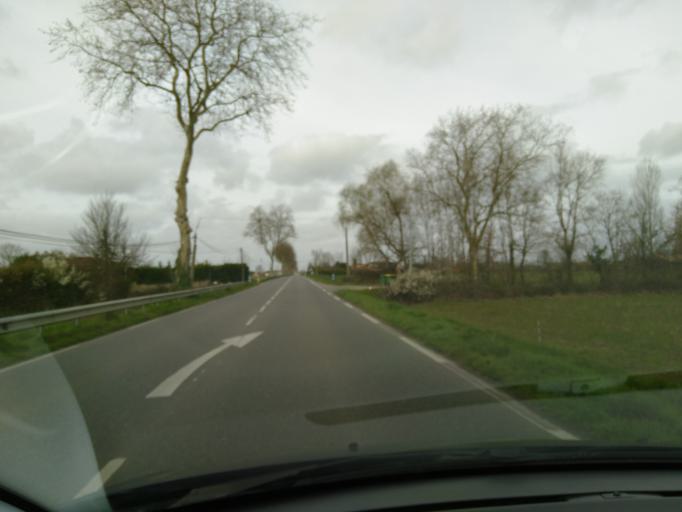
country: FR
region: Midi-Pyrenees
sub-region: Departement de la Haute-Garonne
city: Merville
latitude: 43.7305
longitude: 1.3207
